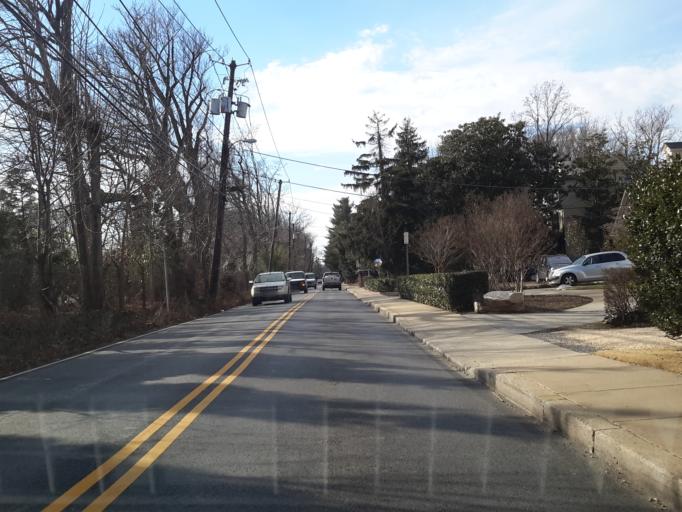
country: US
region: Maryland
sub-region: Montgomery County
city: Chevy Chase
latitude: 38.9767
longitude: -77.0792
